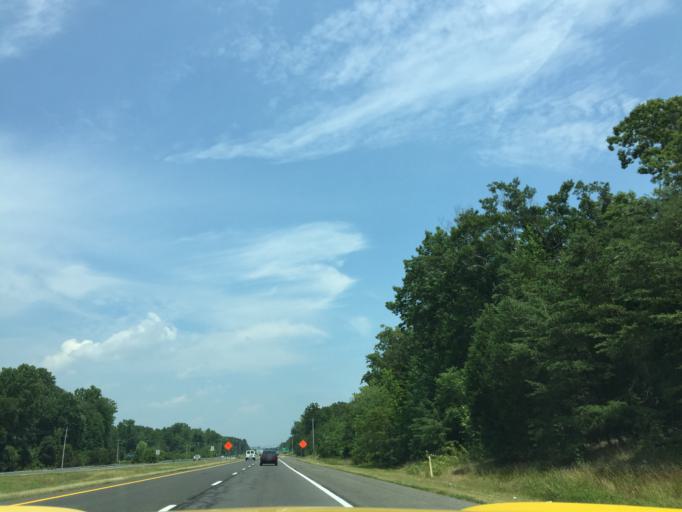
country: US
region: Maryland
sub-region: Prince George's County
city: Accokeek
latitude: 38.6608
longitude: -77.0227
